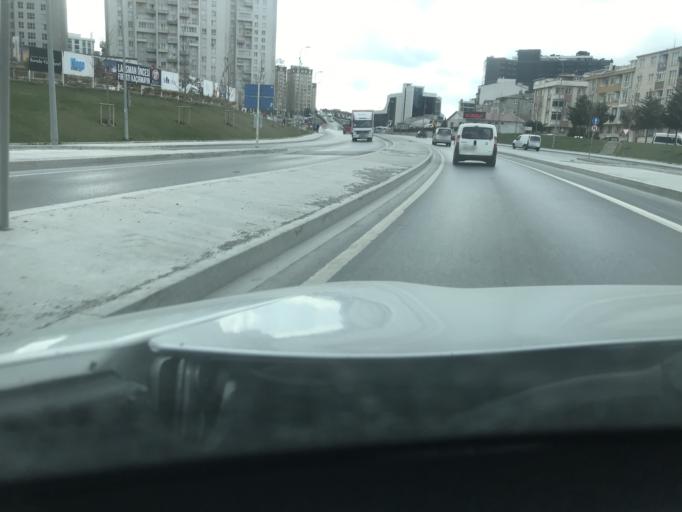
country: TR
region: Istanbul
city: Esenyurt
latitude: 41.0319
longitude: 28.6859
